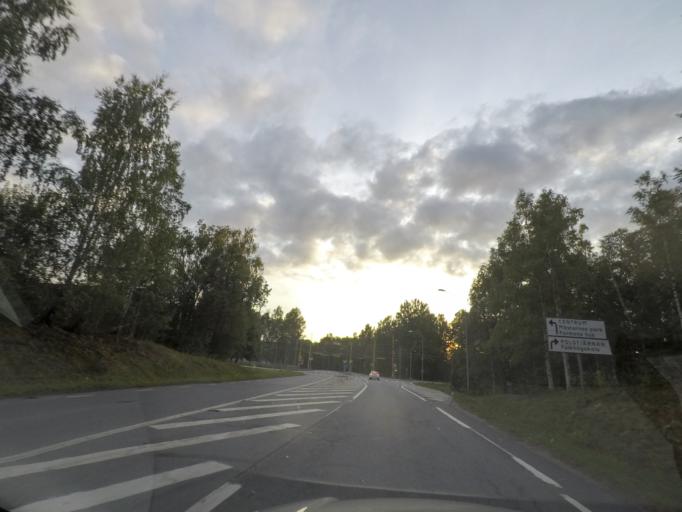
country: SE
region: OErebro
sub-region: Hallefors Kommun
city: Haellefors
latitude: 59.7881
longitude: 14.5219
